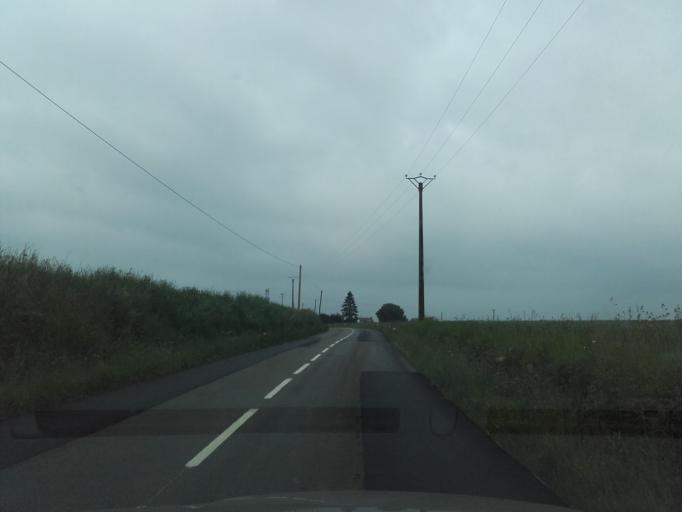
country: FR
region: Pays de la Loire
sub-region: Departement de la Sarthe
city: Saint-Calais
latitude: 47.9083
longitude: 0.7640
